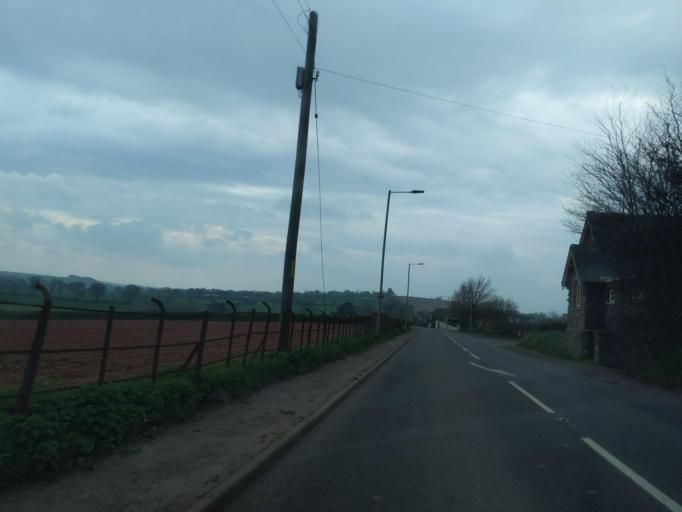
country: GB
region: England
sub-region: Devon
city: Crediton
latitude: 50.8087
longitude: -3.7383
